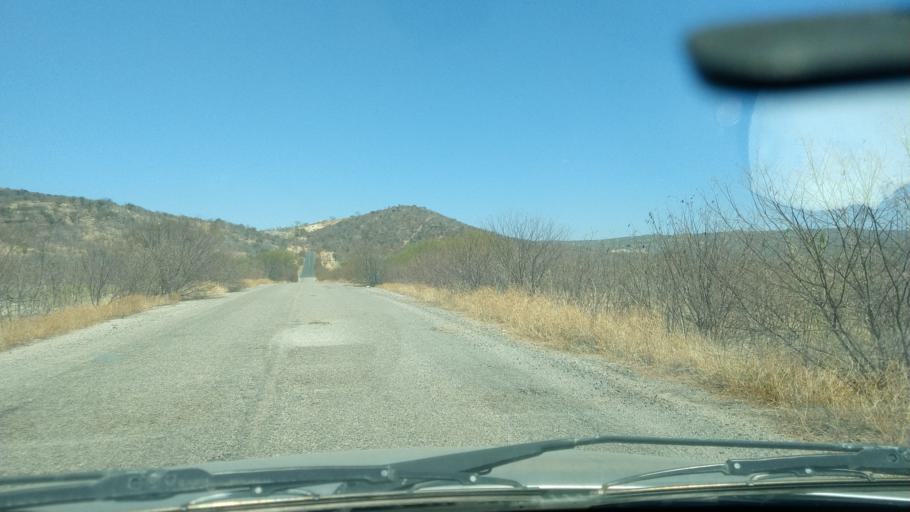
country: BR
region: Rio Grande do Norte
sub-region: Sao Tome
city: Sao Tome
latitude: -5.9725
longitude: -36.1524
